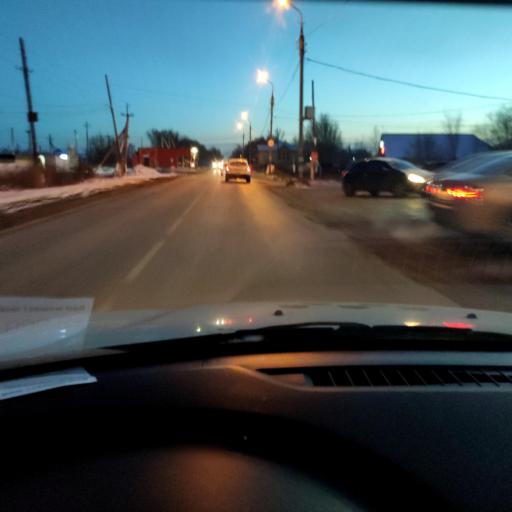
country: RU
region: Samara
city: Tol'yatti
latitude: 53.5569
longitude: 49.3941
